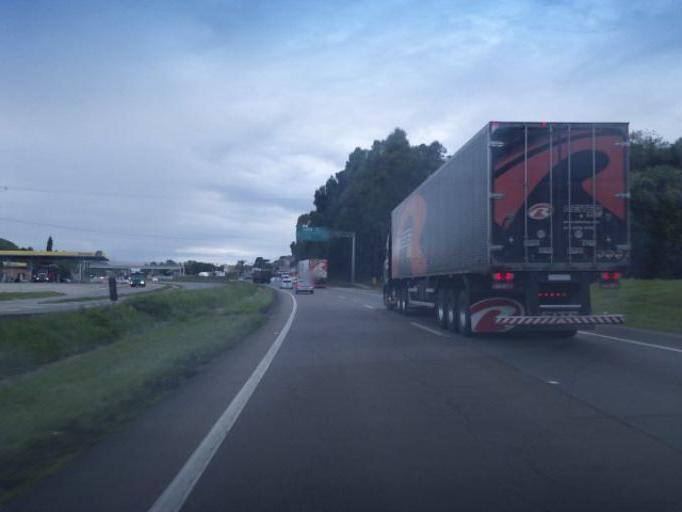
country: BR
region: Parana
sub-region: Sao Jose Dos Pinhais
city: Sao Jose dos Pinhais
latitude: -25.6960
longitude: -49.1448
